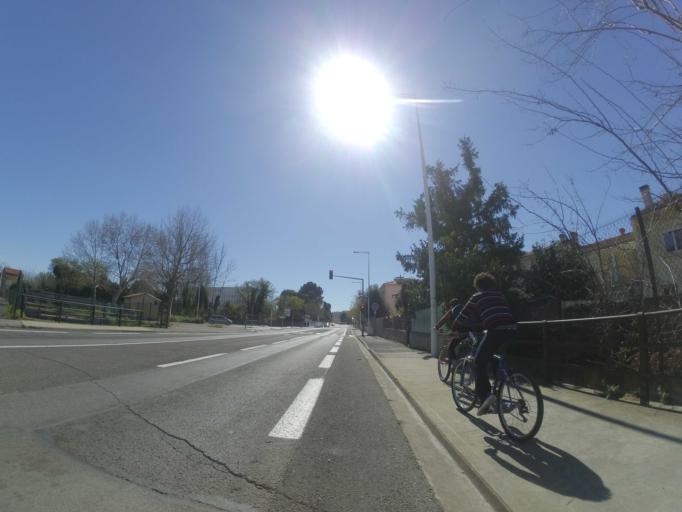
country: FR
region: Languedoc-Roussillon
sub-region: Departement des Pyrenees-Orientales
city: Perpignan
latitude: 42.7138
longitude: 2.8948
